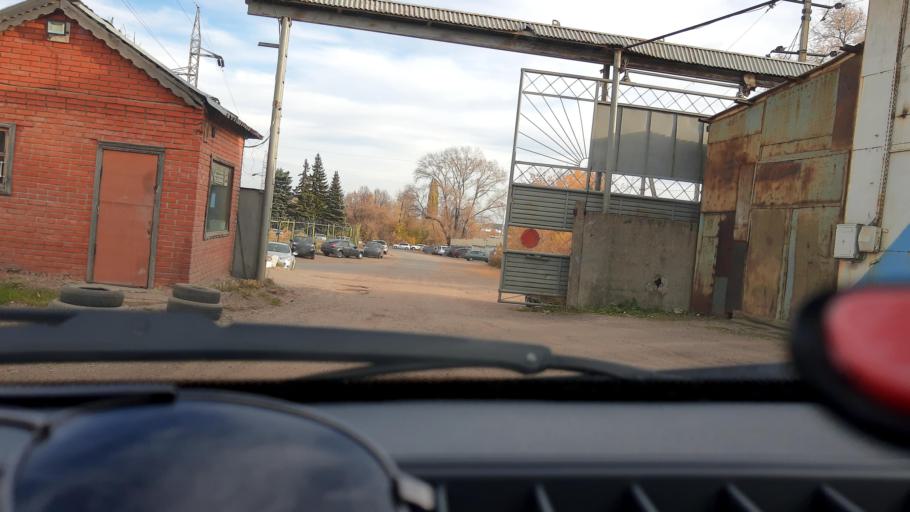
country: RU
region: Bashkortostan
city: Ufa
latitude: 54.8280
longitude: 56.1125
